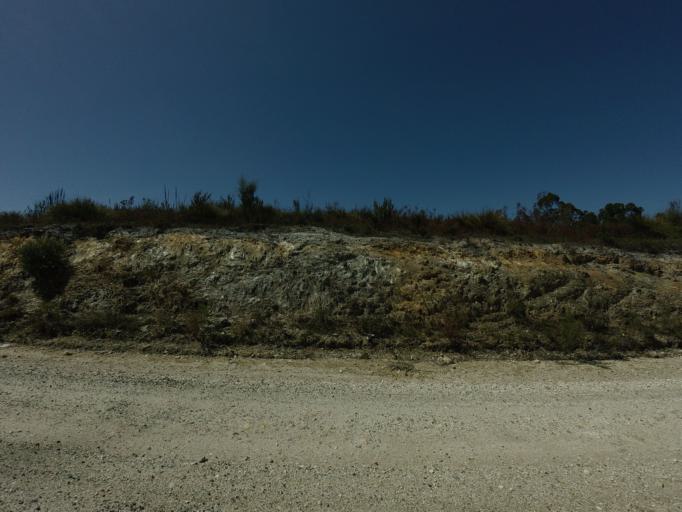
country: AU
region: Tasmania
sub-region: Huon Valley
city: Geeveston
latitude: -43.0255
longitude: 146.3545
